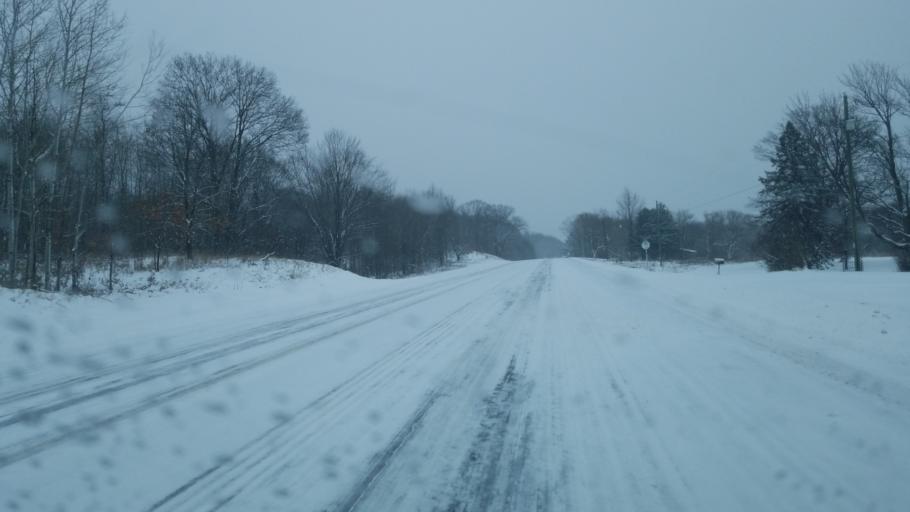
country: US
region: Michigan
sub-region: Osceola County
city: Evart
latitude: 43.8831
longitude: -85.3567
